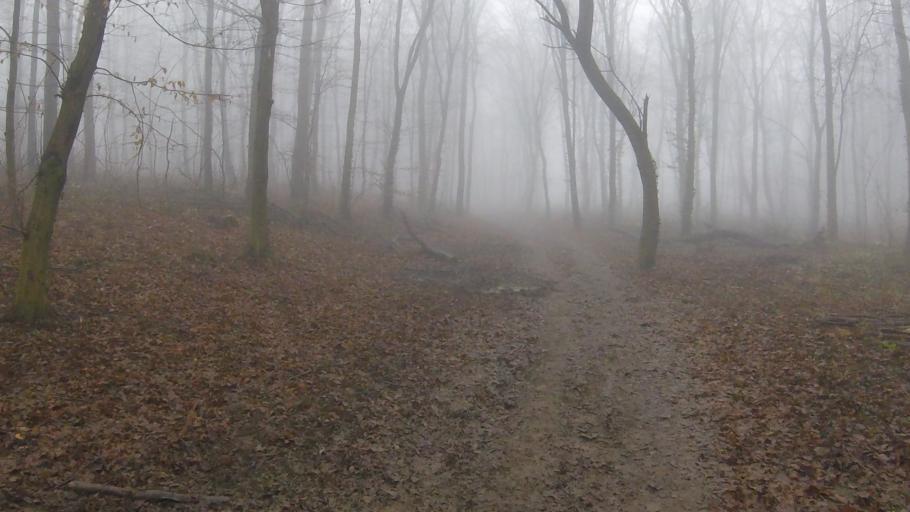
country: HU
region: Pest
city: Budakeszi
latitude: 47.5250
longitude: 18.9376
